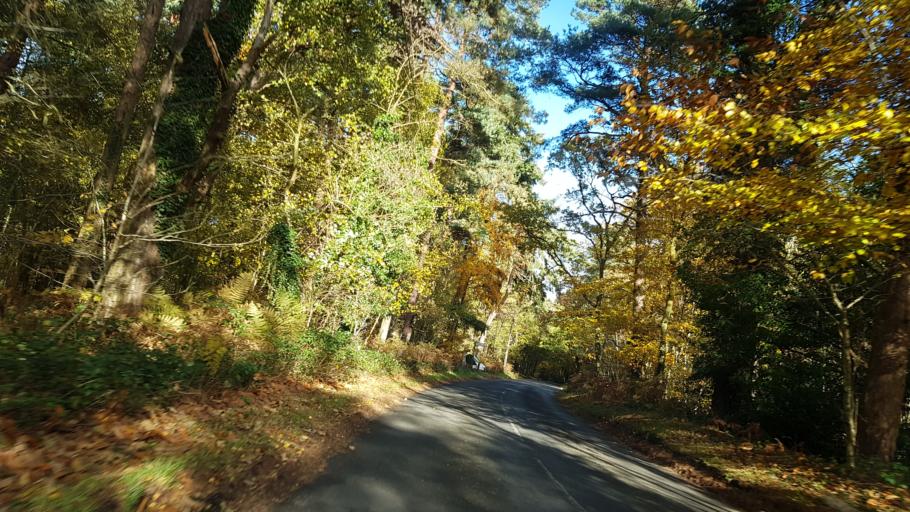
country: GB
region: England
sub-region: Surrey
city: Hindhead
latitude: 51.1508
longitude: -0.7241
